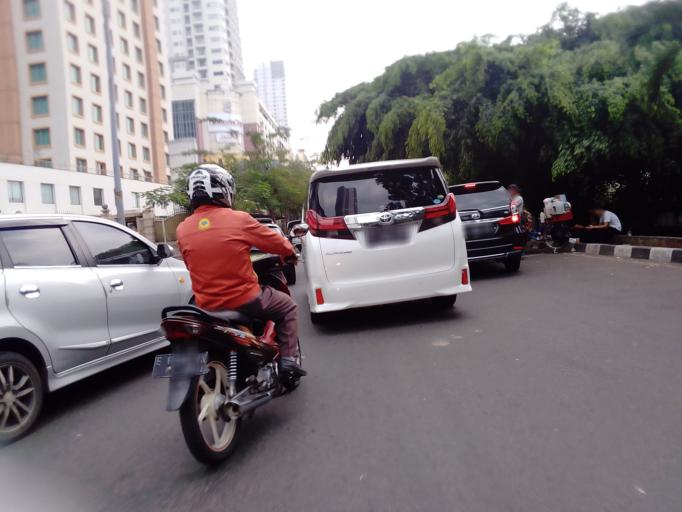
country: ID
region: Jakarta Raya
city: Jakarta
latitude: -6.1943
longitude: 106.8195
